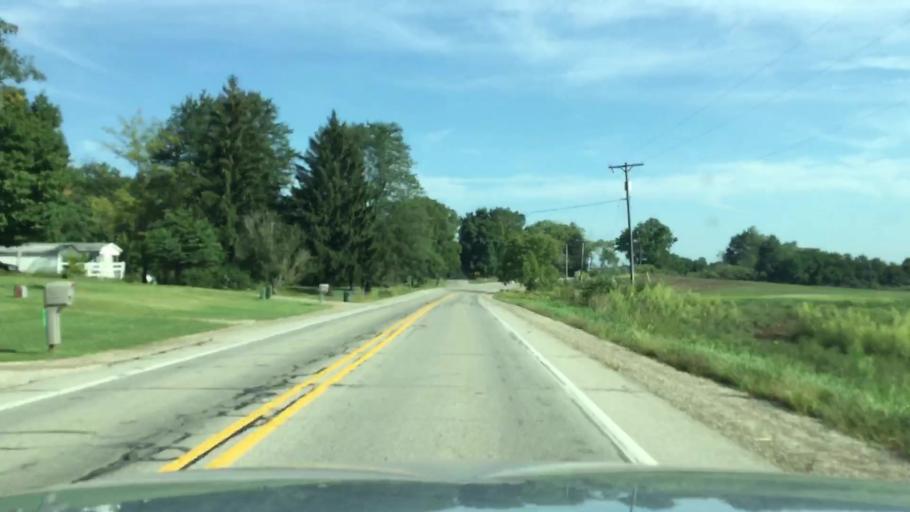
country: US
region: Michigan
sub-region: Lenawee County
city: Manitou Beach-Devils Lake
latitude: 41.9609
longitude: -84.3671
